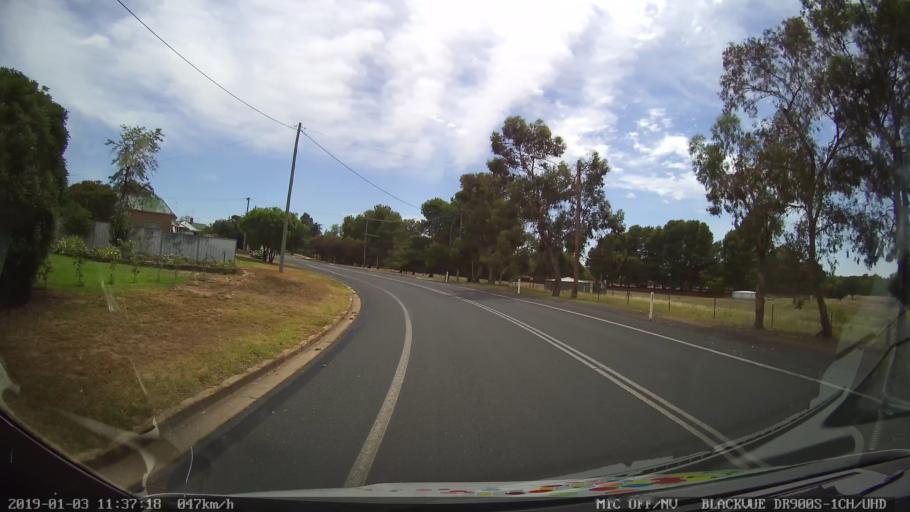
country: AU
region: New South Wales
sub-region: Weddin
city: Grenfell
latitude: -33.9039
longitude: 148.1609
